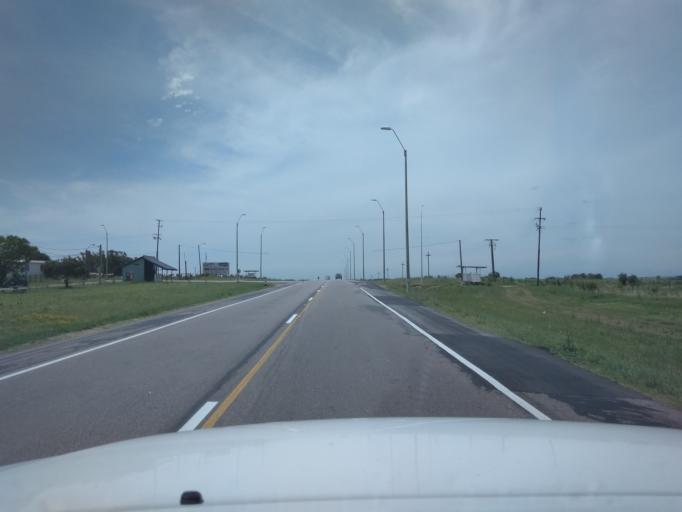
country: UY
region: Florida
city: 25 de Mayo
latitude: -34.2387
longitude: -56.2132
